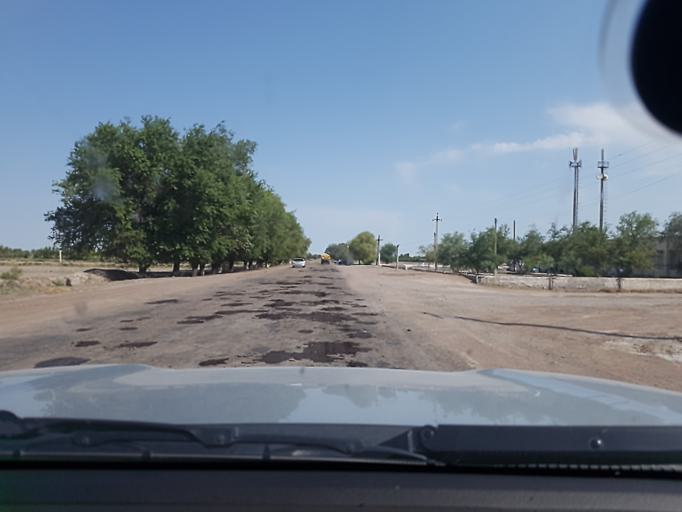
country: UZ
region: Karakalpakstan
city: Khujayli
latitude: 42.2209
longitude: 59.4890
